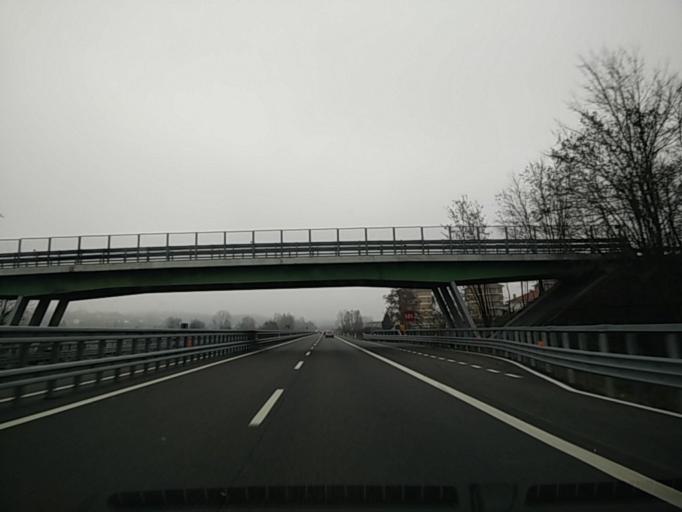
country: IT
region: Piedmont
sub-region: Provincia di Asti
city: Villafranca d'Asti
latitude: 44.9162
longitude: 8.0346
